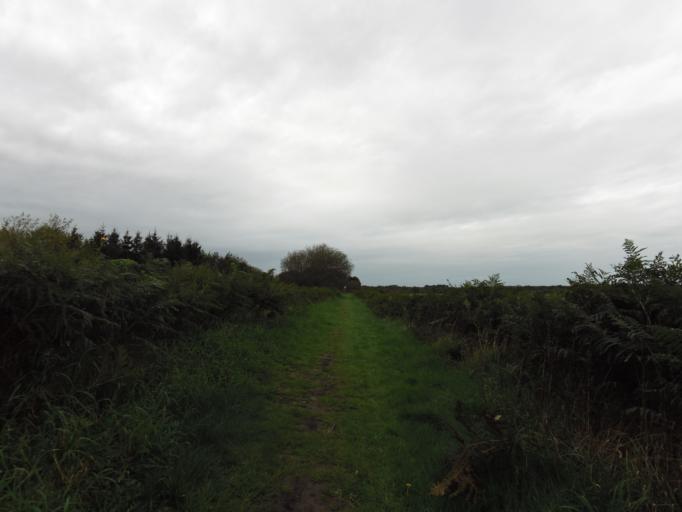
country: IE
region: Leinster
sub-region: Uibh Fhaili
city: Ferbane
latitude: 53.2135
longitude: -7.7305
